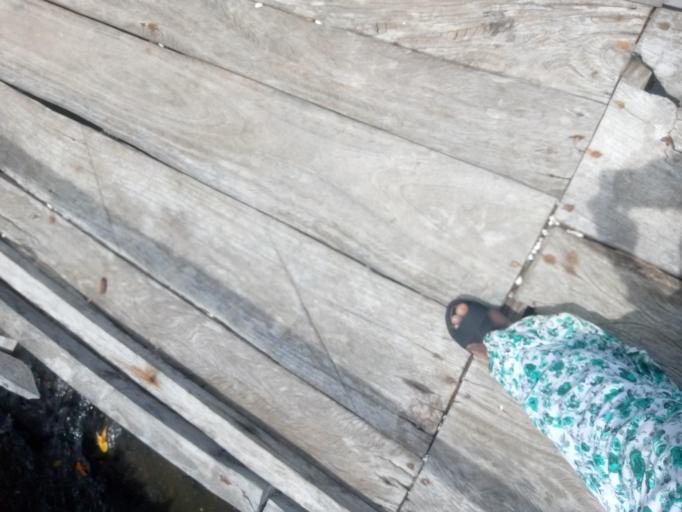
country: GM
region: Western
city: Gunjur
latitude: 13.0389
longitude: -16.7352
